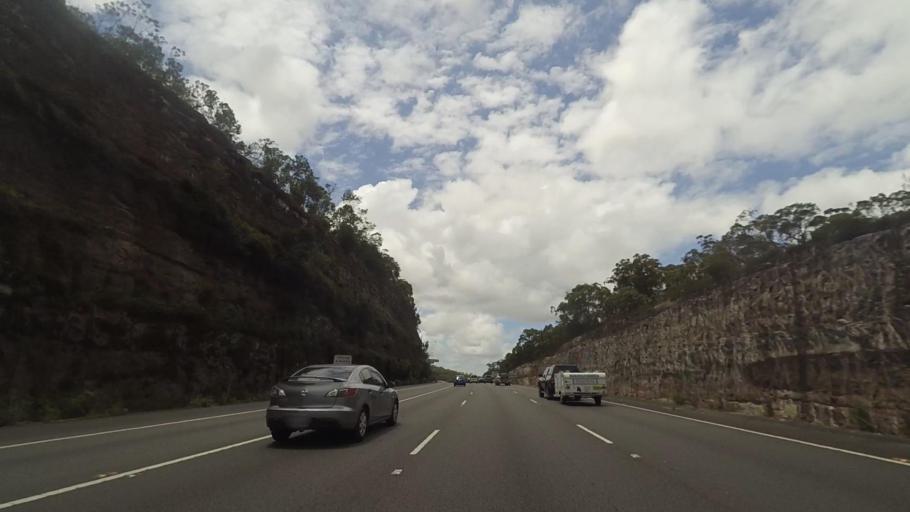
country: AU
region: New South Wales
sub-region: Gosford Shire
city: Point Clare
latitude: -33.4575
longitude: 151.2032
